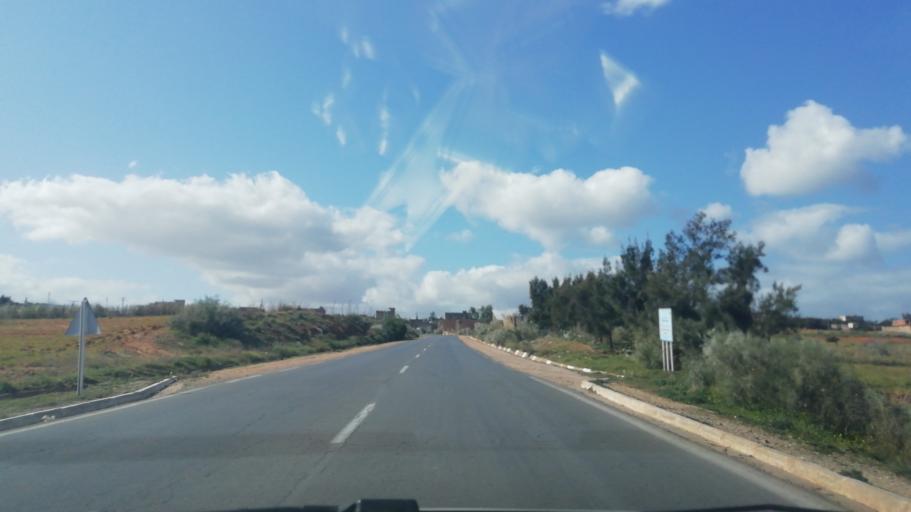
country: DZ
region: Relizane
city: Mazouna
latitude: 36.2892
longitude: 0.6492
